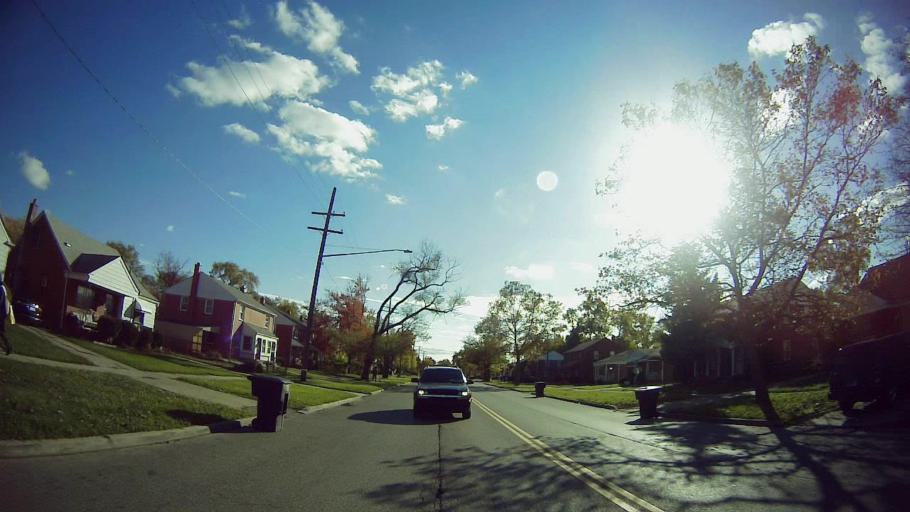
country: US
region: Michigan
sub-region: Wayne County
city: Dearborn Heights
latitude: 42.3601
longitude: -83.2360
